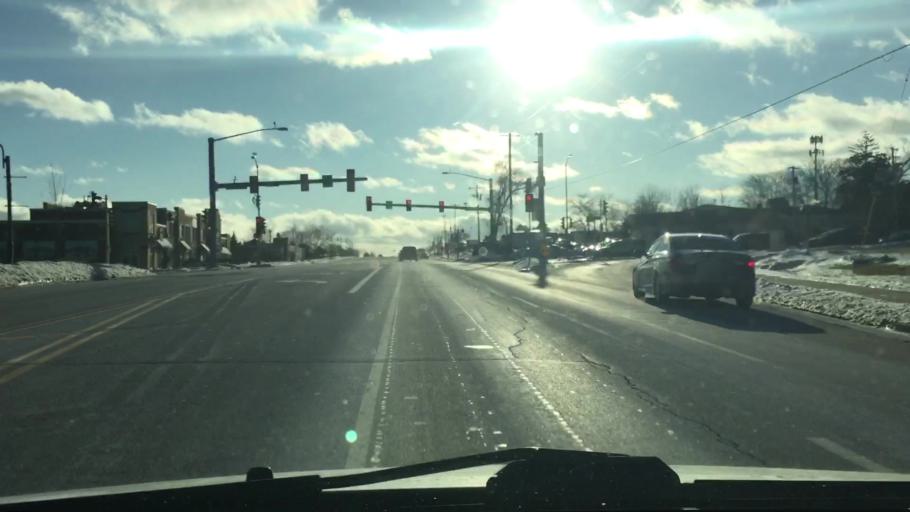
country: US
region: Wisconsin
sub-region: Waukesha County
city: New Berlin
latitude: 42.9811
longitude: -88.1020
